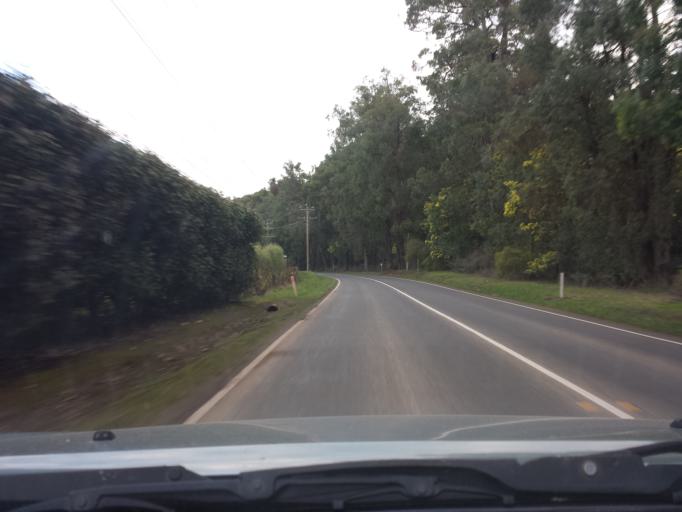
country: AU
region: Victoria
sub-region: Yarra Ranges
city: Monbulk
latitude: -37.8415
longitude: 145.4252
